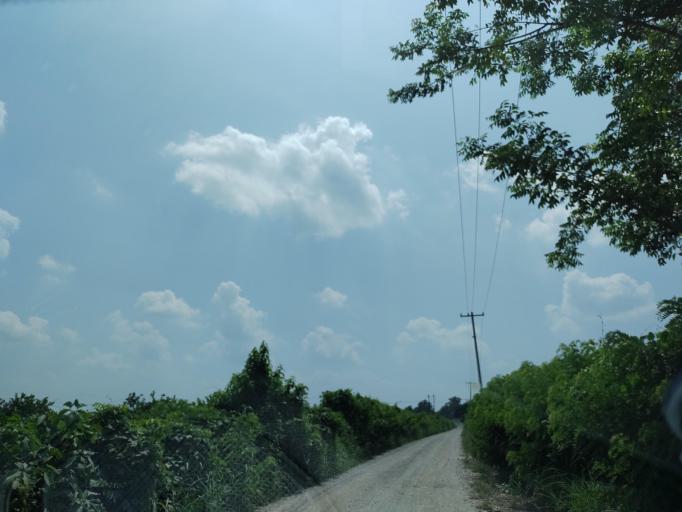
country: MX
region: Veracruz
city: Martinez de la Torre
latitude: 20.0874
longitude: -97.0377
